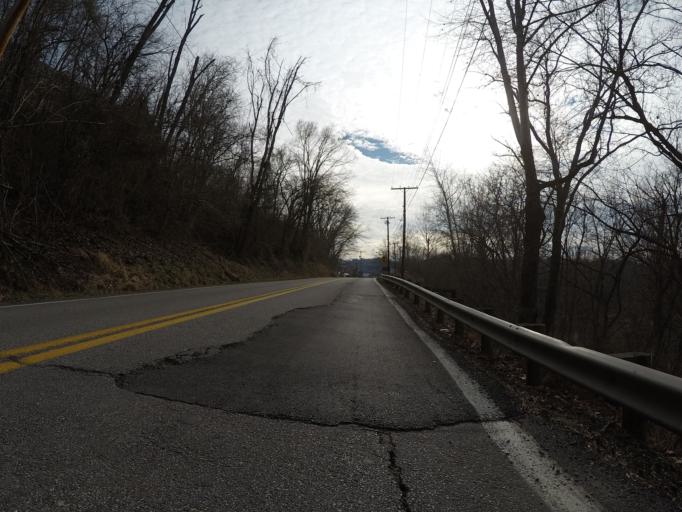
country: US
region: West Virginia
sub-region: Cabell County
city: Barboursville
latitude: 38.4118
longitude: -82.2954
